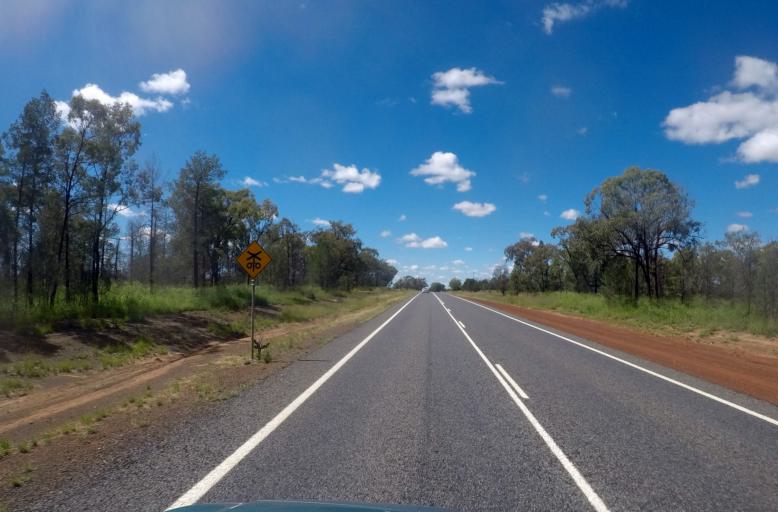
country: AU
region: Queensland
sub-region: Western Downs
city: Westcourt
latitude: -26.6471
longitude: 150.0722
